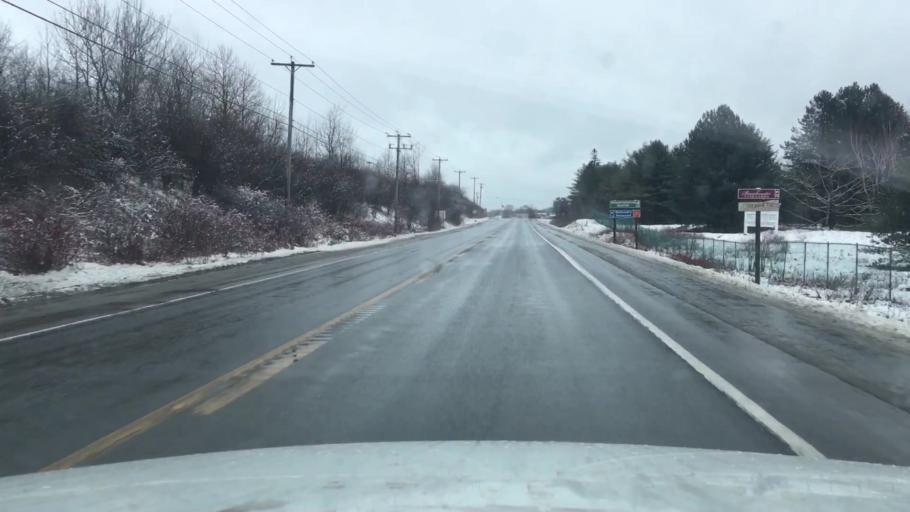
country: US
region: Maine
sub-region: Knox County
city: Thomaston
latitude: 44.0902
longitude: -69.1495
